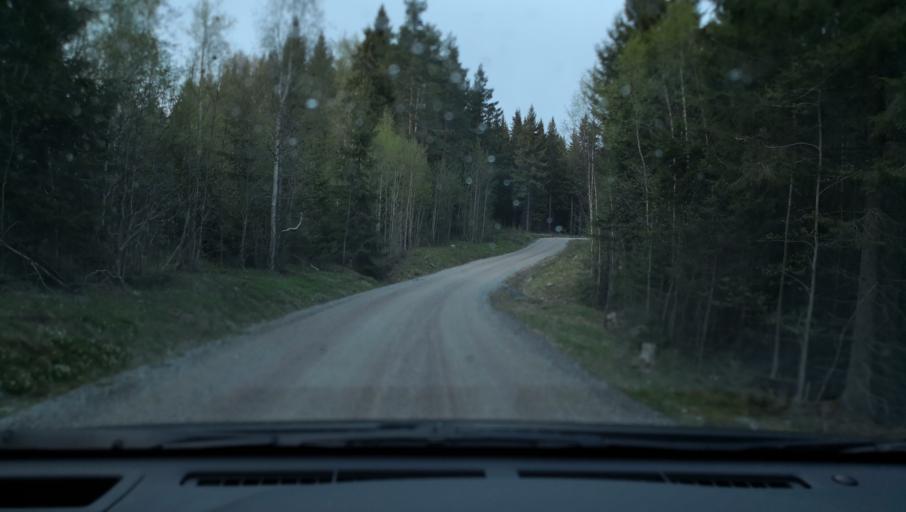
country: SE
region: Dalarna
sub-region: Saters Kommun
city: Saeter
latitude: 60.1816
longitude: 15.7280
